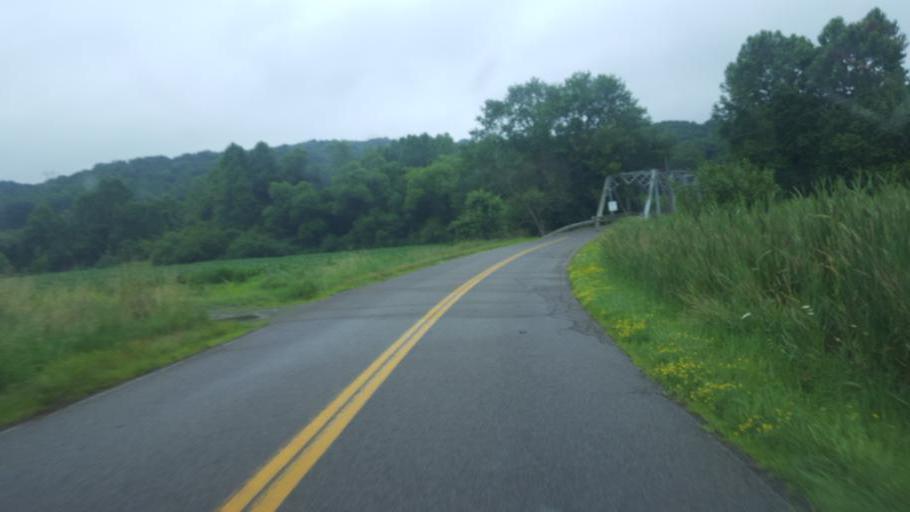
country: US
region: Ohio
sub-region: Columbiana County
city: Salineville
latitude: 40.5210
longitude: -80.8618
